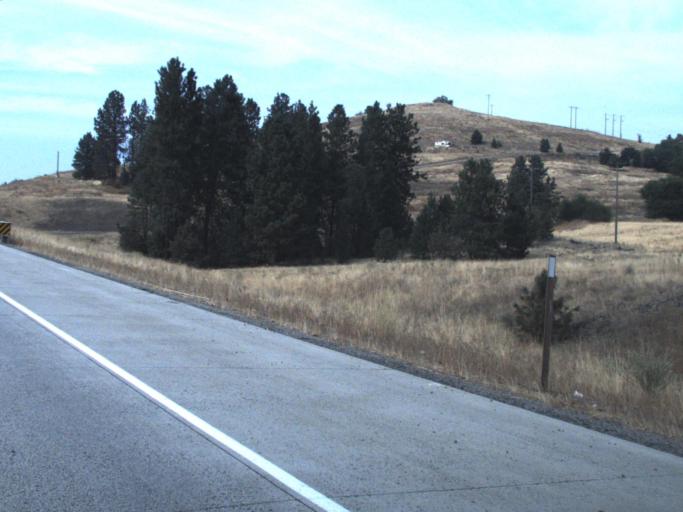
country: US
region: Washington
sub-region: Adams County
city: Ritzville
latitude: 47.1095
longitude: -118.3972
